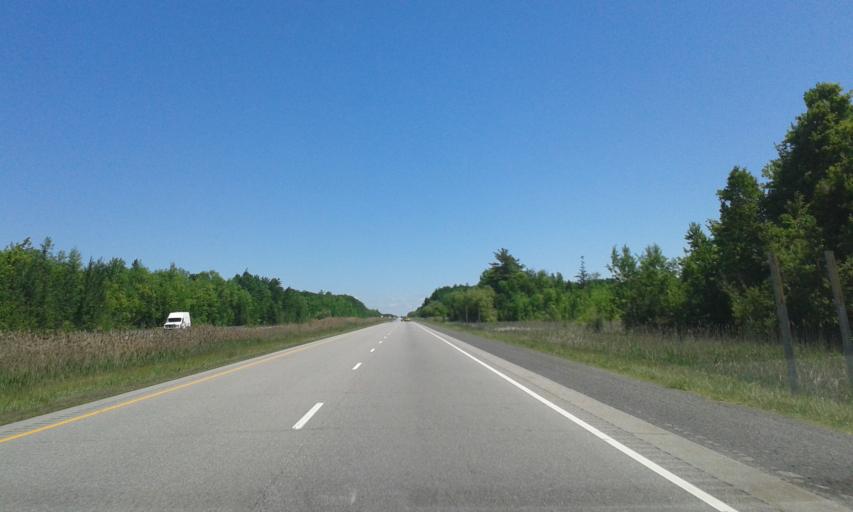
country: CA
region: Ontario
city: Prescott
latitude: 44.7819
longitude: -75.4509
